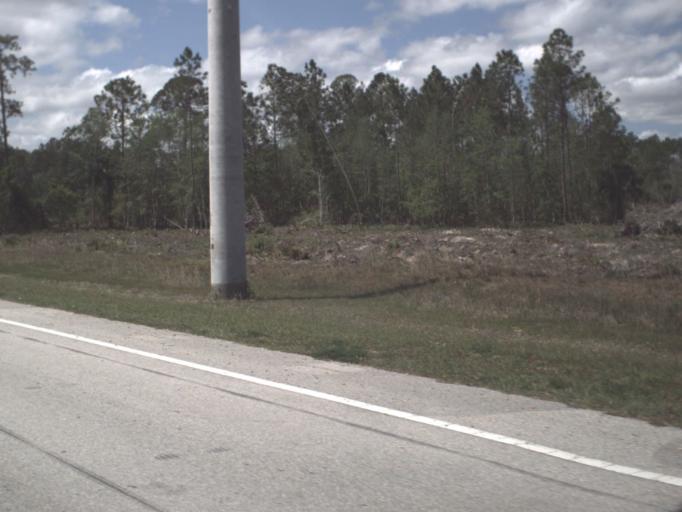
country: US
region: Florida
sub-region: Flagler County
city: Bunnell
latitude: 29.5120
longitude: -81.2641
